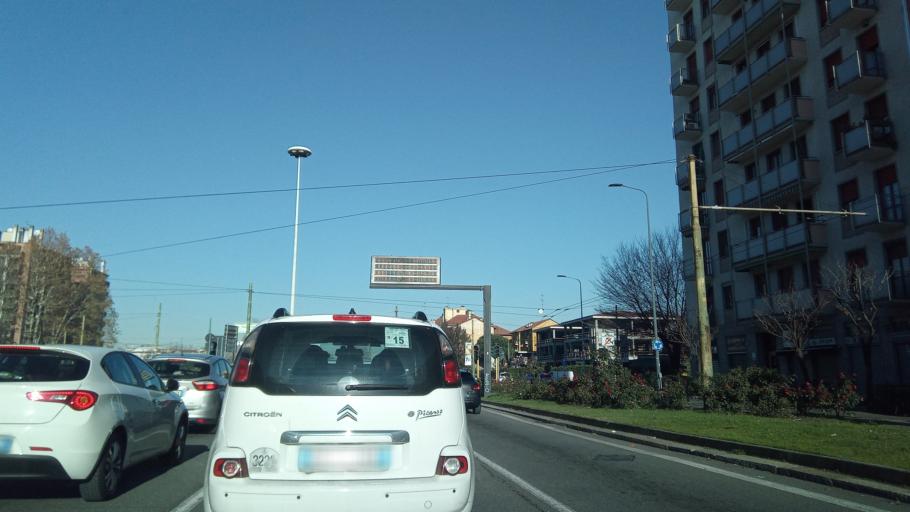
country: IT
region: Lombardy
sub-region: Citta metropolitana di Milano
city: Chiaravalle
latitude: 45.4437
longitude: 9.2243
